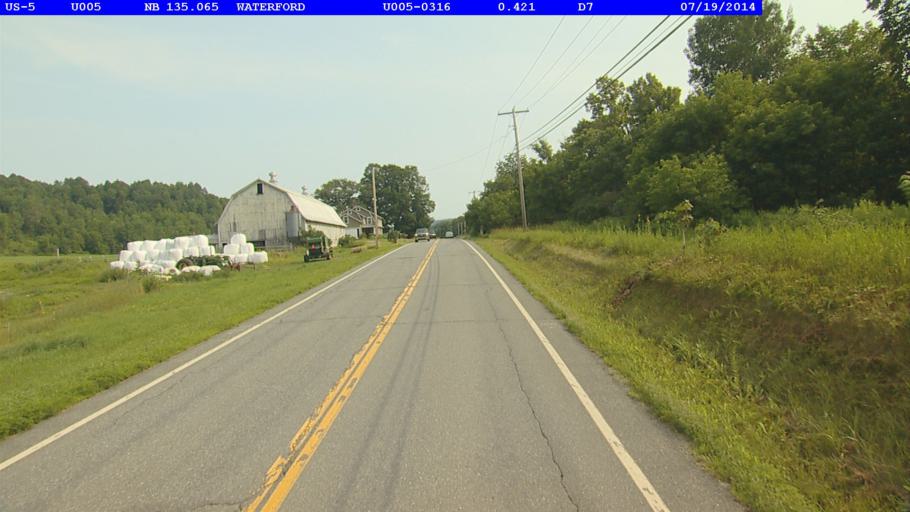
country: US
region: Vermont
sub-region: Caledonia County
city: Saint Johnsbury
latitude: 44.3852
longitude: -72.0261
